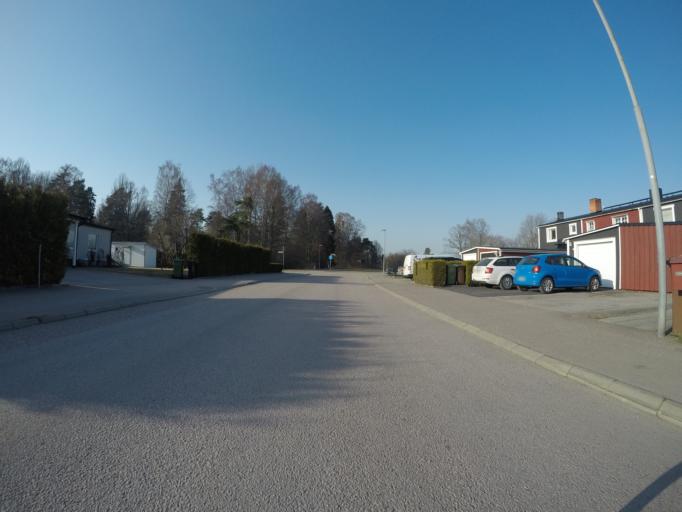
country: SE
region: Vaestmanland
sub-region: Kungsors Kommun
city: Kungsoer
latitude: 59.4221
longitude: 16.1126
